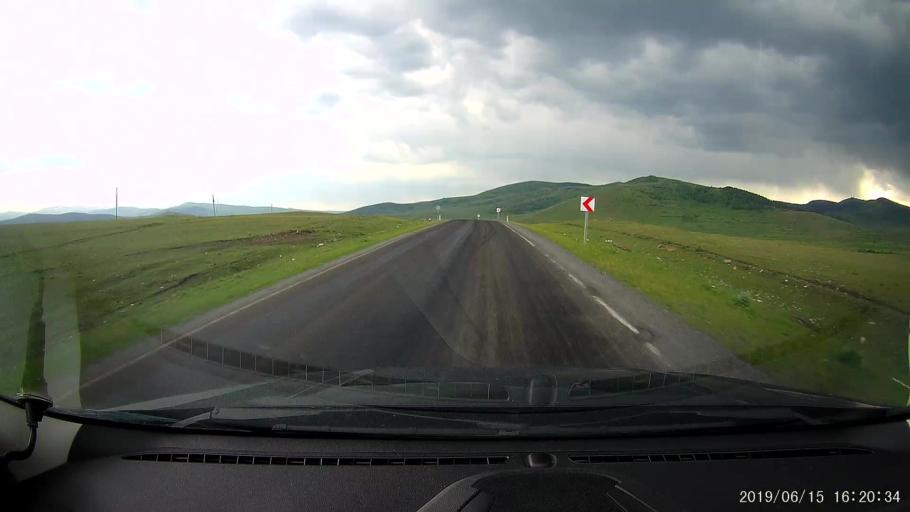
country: TR
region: Ardahan
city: Hanak
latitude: 41.2121
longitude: 42.8471
